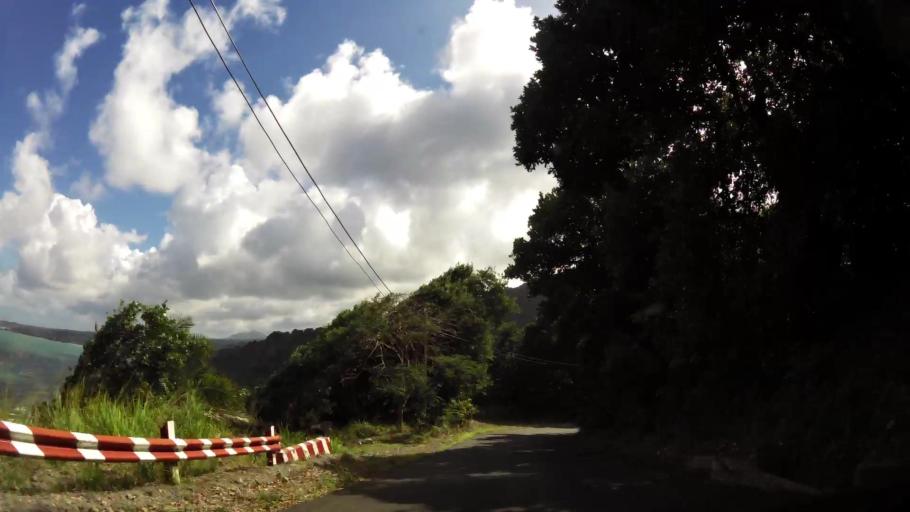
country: DM
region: Saint Andrew
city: Calibishie
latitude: 15.6174
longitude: -61.4073
